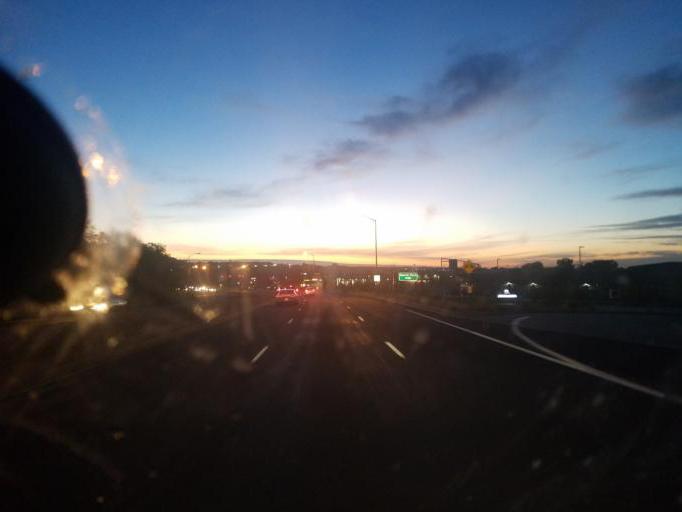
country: US
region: Colorado
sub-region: El Paso County
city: Stratmoor
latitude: 38.7959
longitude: -104.7930
